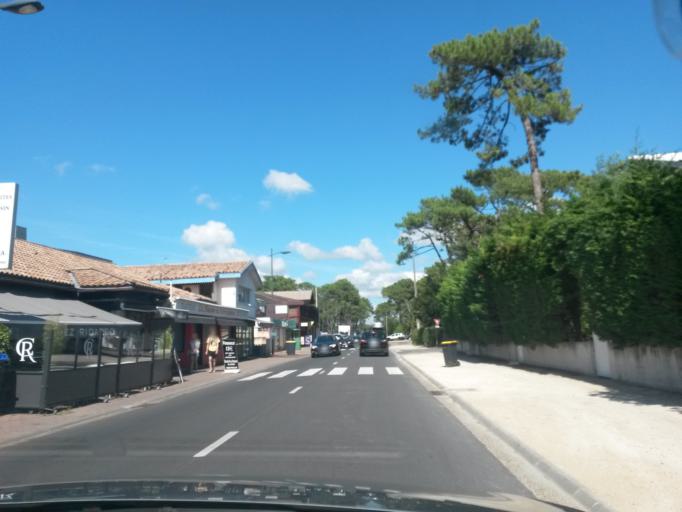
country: FR
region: Aquitaine
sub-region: Departement de la Gironde
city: Arcachon
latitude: 44.7026
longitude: -1.2282
